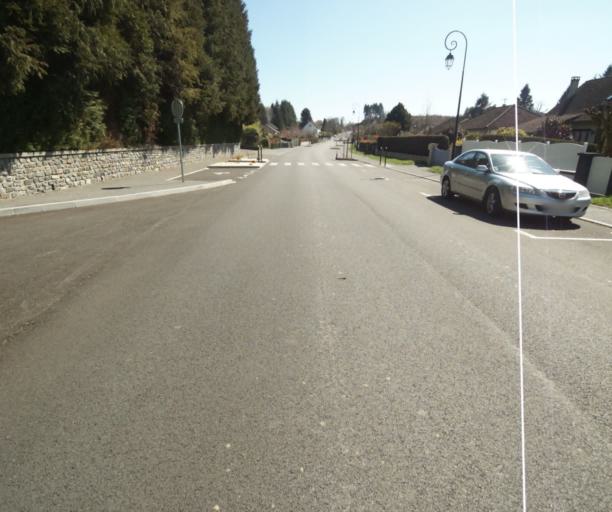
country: FR
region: Limousin
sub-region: Departement de la Correze
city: Saint-Mexant
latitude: 45.2826
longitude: 1.6587
